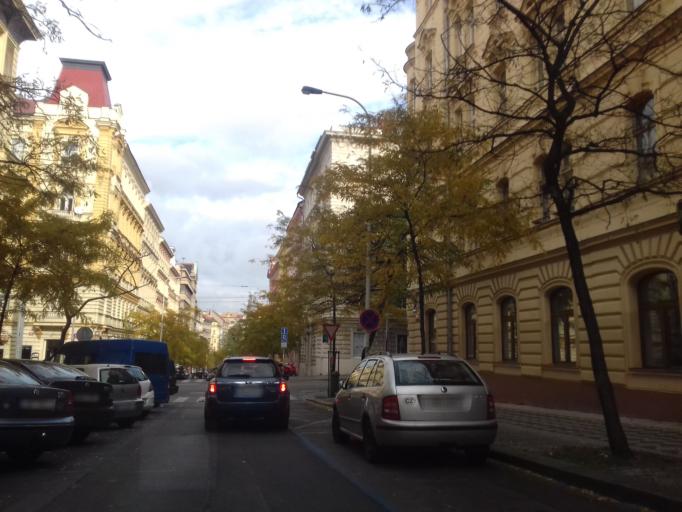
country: CZ
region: Praha
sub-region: Praha 8
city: Karlin
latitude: 50.0750
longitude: 14.4420
